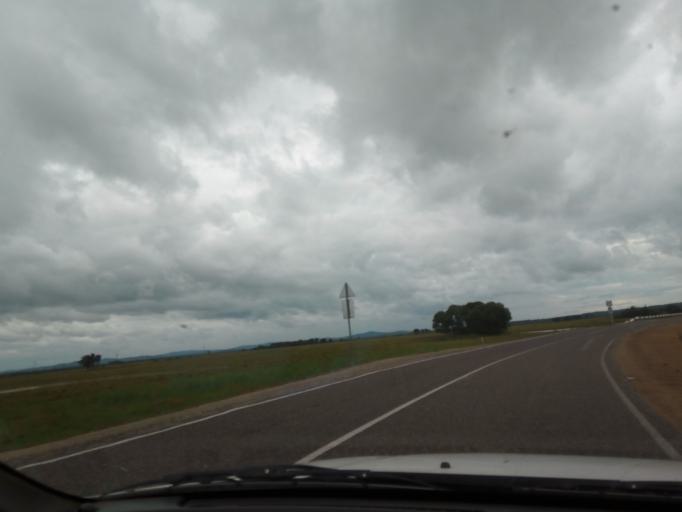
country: RU
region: Primorskiy
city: Dal'nerechensk
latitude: 45.9159
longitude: 133.7714
